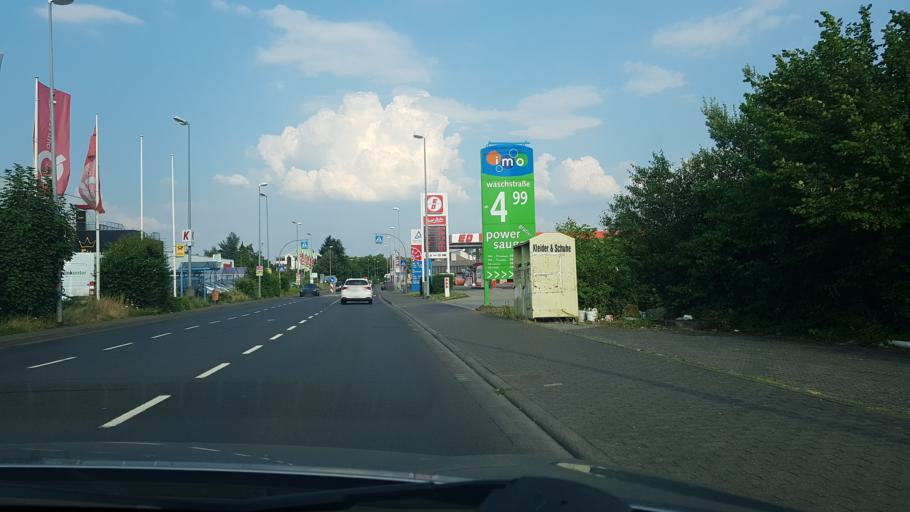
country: DE
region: Rheinland-Pfalz
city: Kaltenengers
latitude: 50.3945
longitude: 7.5347
